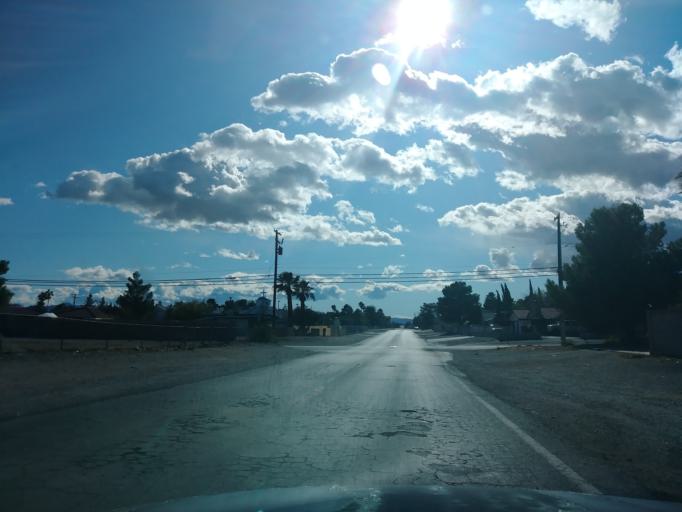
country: US
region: Nevada
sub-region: Clark County
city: Spring Valley
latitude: 36.1504
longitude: -115.2168
